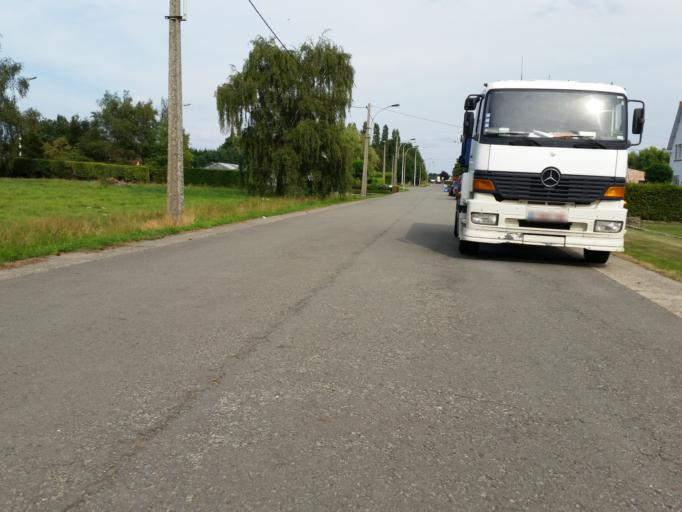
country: BE
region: Flanders
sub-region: Provincie Antwerpen
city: Rumst
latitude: 51.0938
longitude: 4.4426
